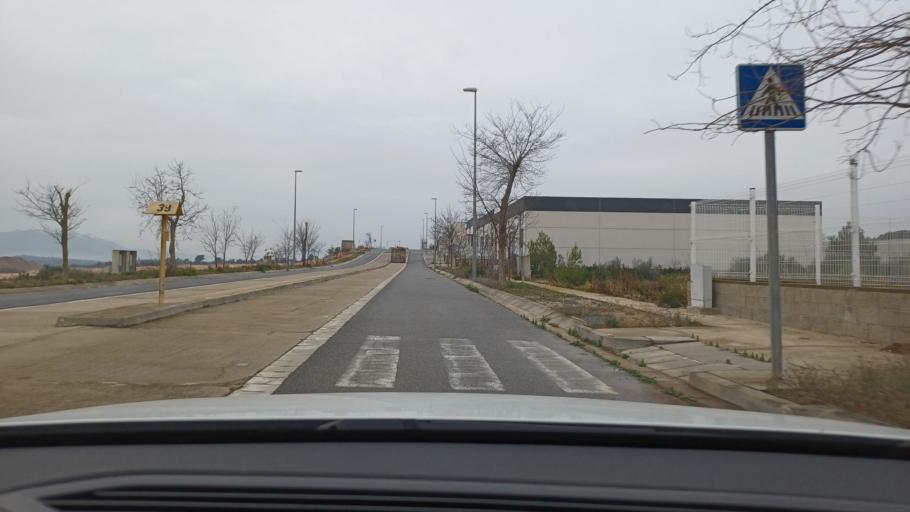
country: ES
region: Catalonia
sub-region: Provincia de Tarragona
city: Amposta
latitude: 40.7673
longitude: 0.5952
